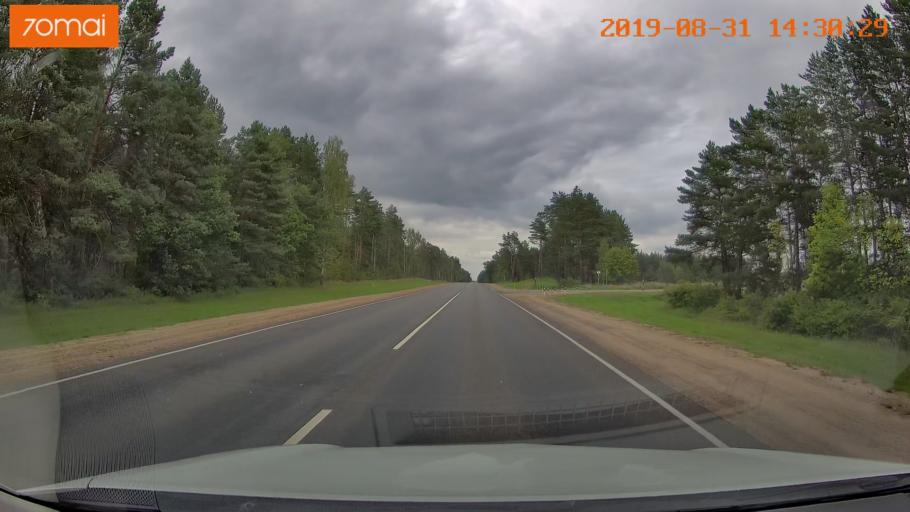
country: RU
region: Smolensk
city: Yekimovichi
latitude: 54.1317
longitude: 33.3514
